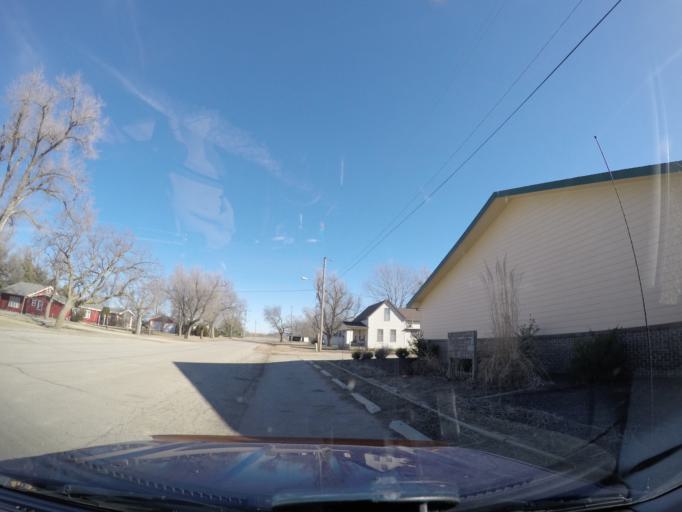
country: US
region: Kansas
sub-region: Marion County
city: Marion
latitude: 38.4955
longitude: -96.9600
